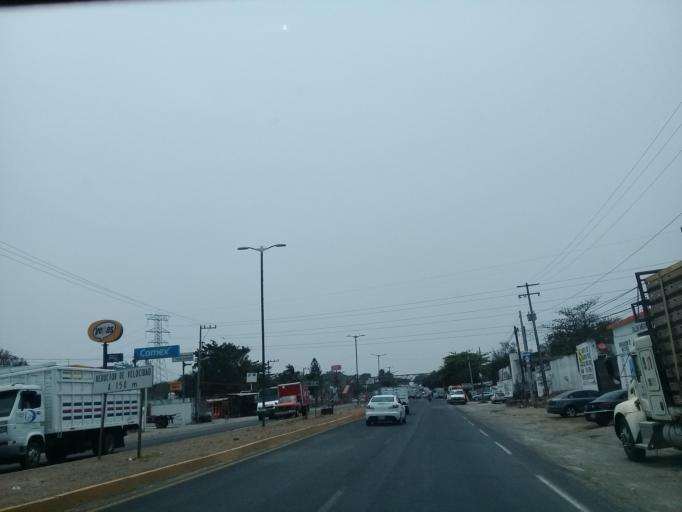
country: MX
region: Veracruz
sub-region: Veracruz
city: Las Amapolas
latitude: 19.1637
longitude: -96.2105
